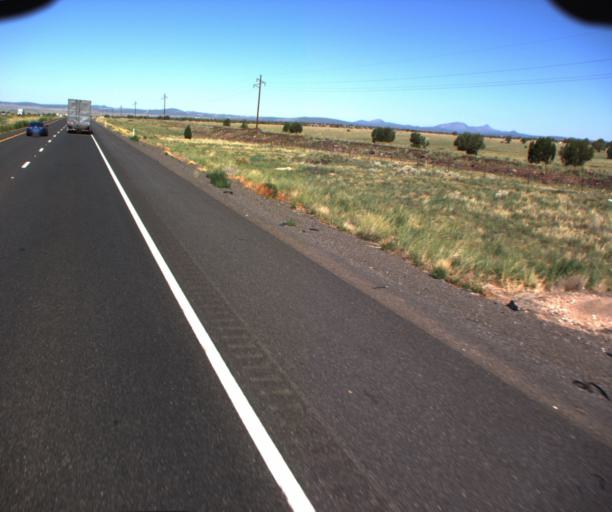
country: US
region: Arizona
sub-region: Yavapai County
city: Paulden
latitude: 35.2230
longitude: -112.5517
